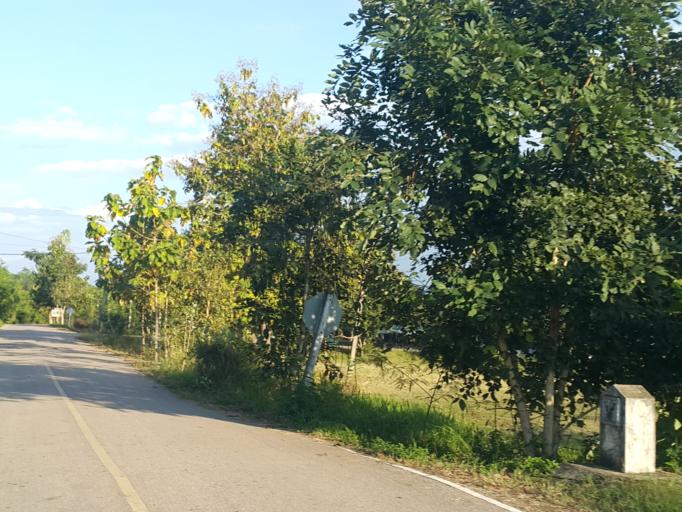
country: TH
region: Lampang
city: Lampang
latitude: 18.4221
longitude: 99.5422
